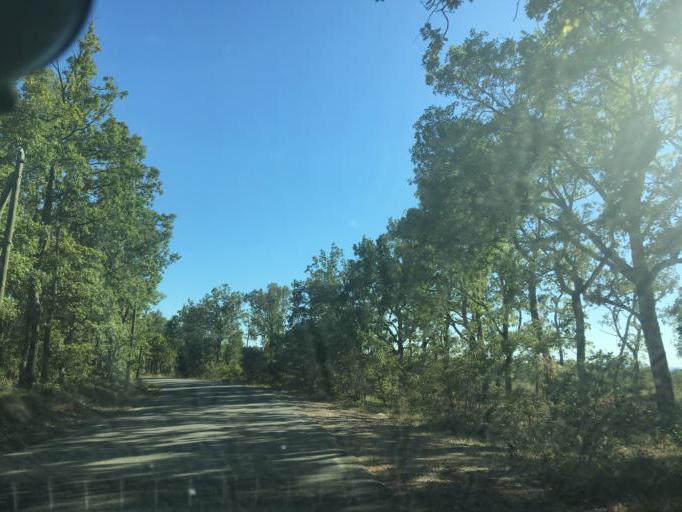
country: FR
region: Provence-Alpes-Cote d'Azur
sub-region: Departement du Var
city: Regusse
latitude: 43.6812
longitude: 6.1580
